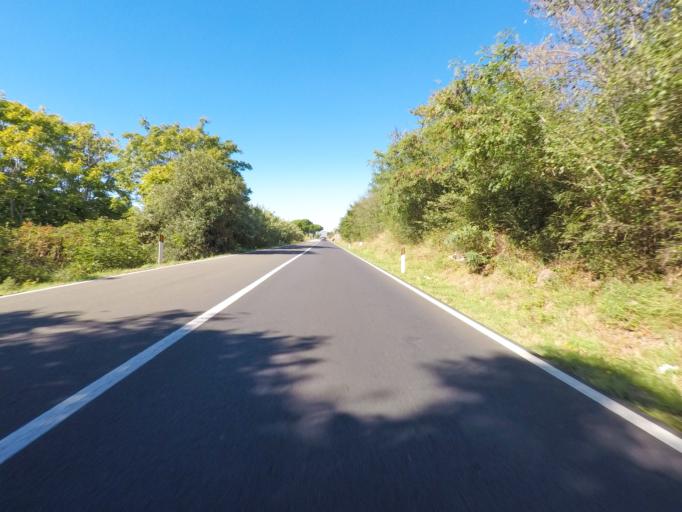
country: IT
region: Tuscany
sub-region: Provincia di Grosseto
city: Orbetello Scalo
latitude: 42.4531
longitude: 11.2527
